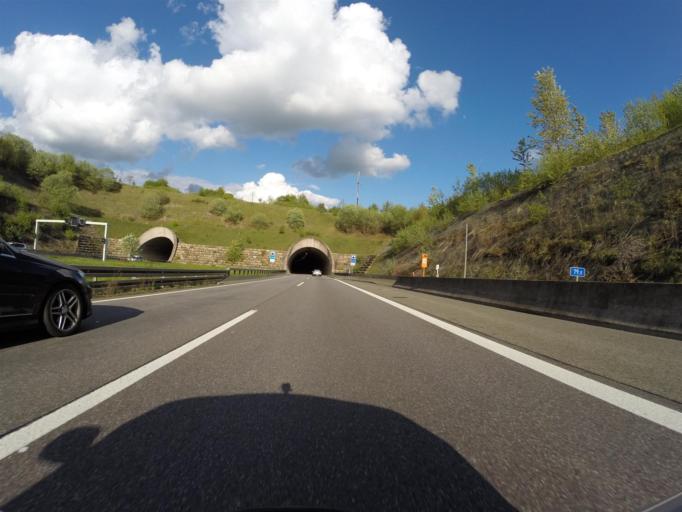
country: DE
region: Saarland
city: Orscholz
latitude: 49.4495
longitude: 6.5078
